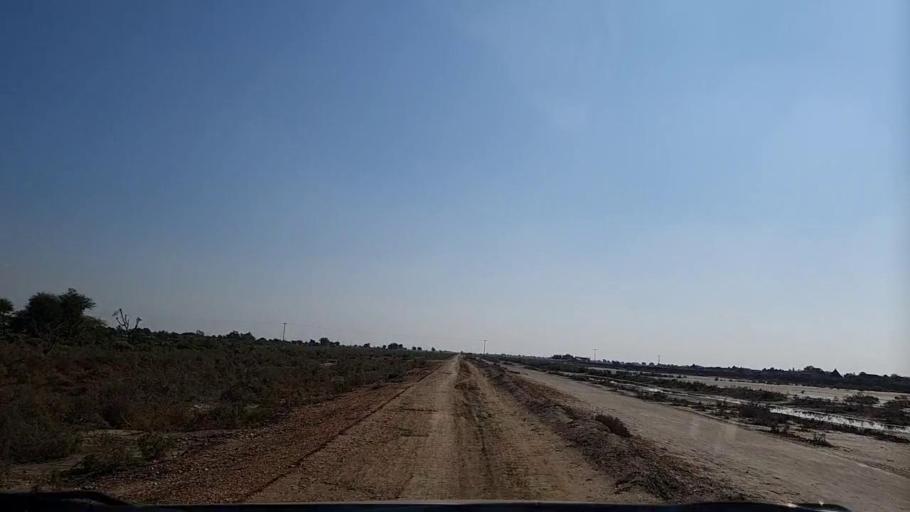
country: PK
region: Sindh
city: Pithoro
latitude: 25.7060
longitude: 69.3368
